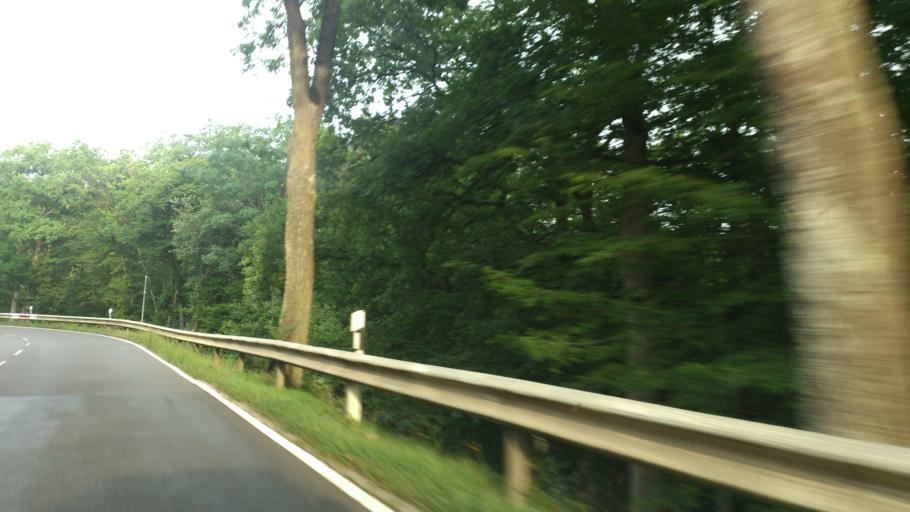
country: DE
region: Rheinland-Pfalz
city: Dorsel
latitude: 50.3669
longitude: 6.7852
